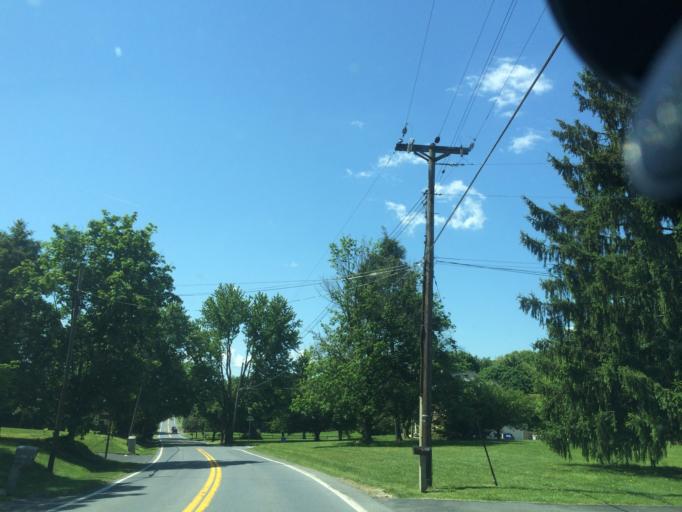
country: US
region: Maryland
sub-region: Carroll County
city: Sykesville
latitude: 39.4070
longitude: -77.0167
